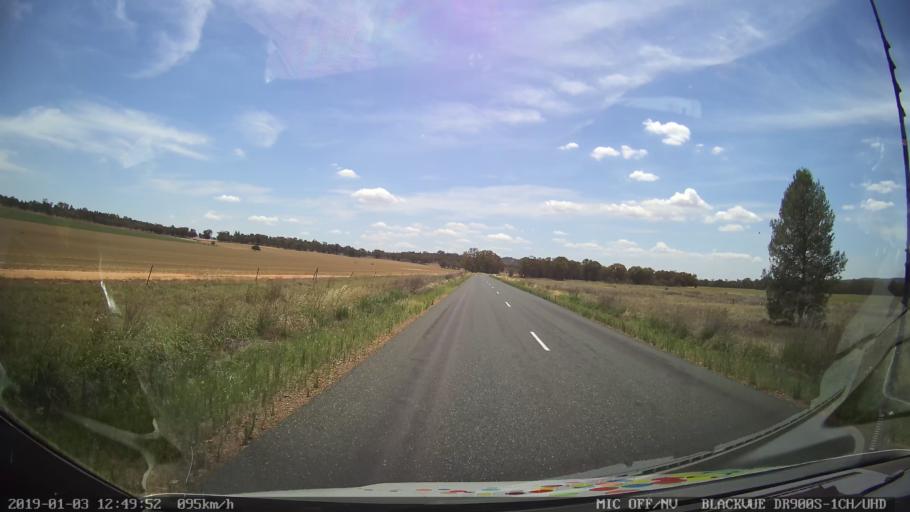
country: AU
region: New South Wales
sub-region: Weddin
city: Grenfell
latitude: -33.6979
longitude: 148.2646
